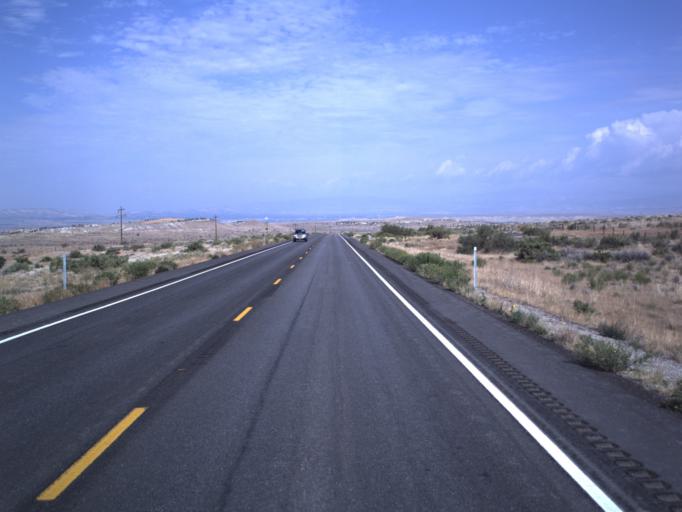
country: US
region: Utah
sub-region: Uintah County
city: Naples
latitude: 40.3308
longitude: -109.2797
